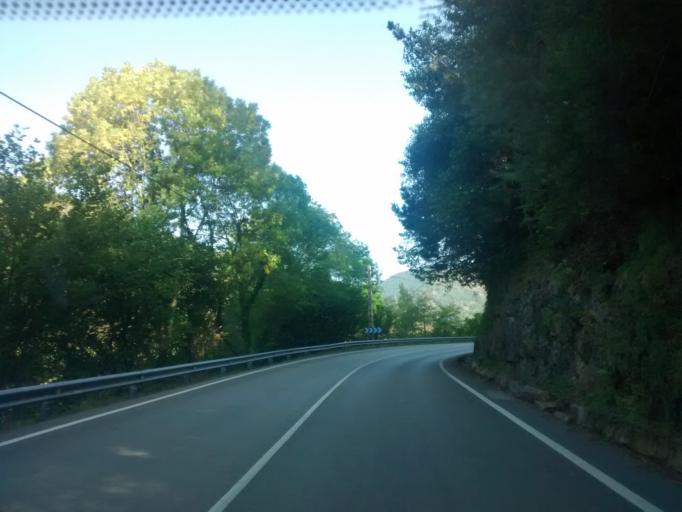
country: ES
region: Cantabria
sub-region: Provincia de Cantabria
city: Ruente
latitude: 43.1721
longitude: -4.2937
